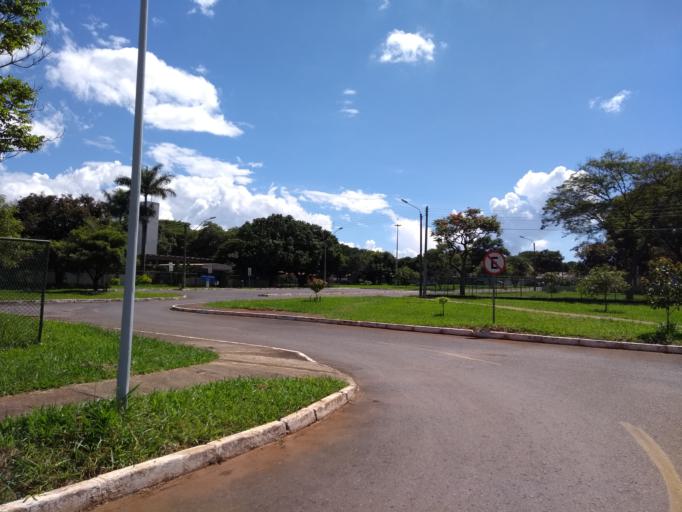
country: BR
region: Federal District
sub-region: Brasilia
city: Brasilia
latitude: -15.7840
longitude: -47.9365
